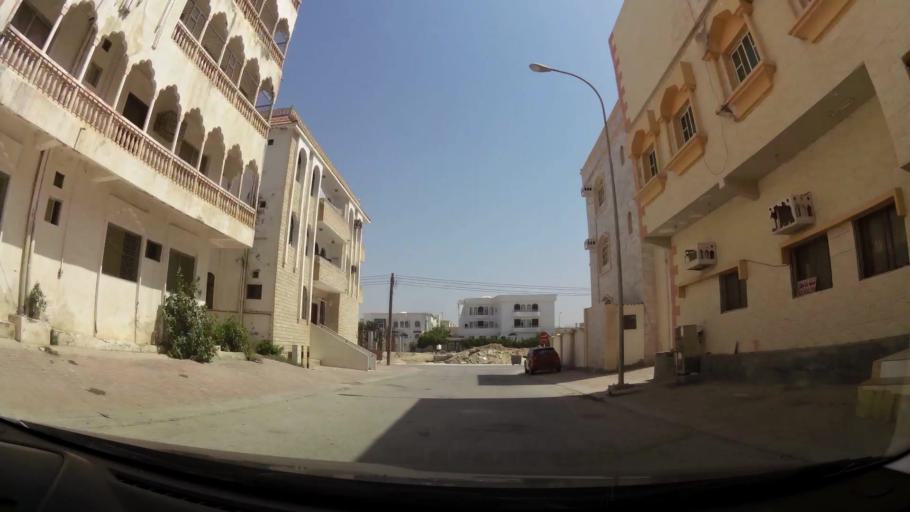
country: OM
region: Zufar
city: Salalah
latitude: 17.0209
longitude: 54.1081
